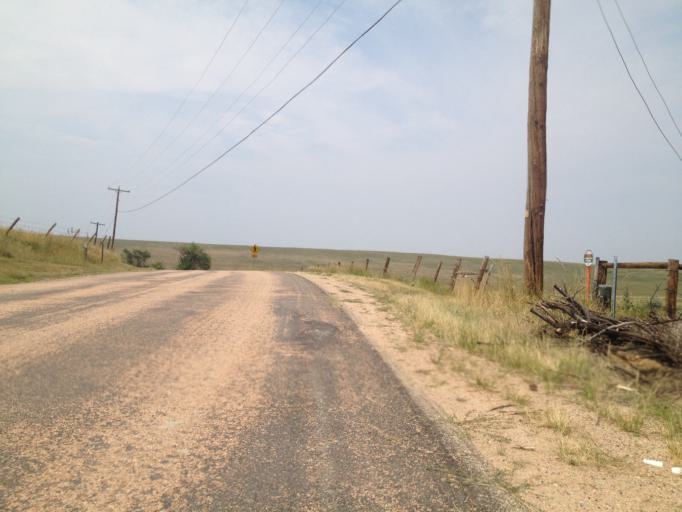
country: US
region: Colorado
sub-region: Boulder County
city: Superior
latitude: 39.9573
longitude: -105.1988
